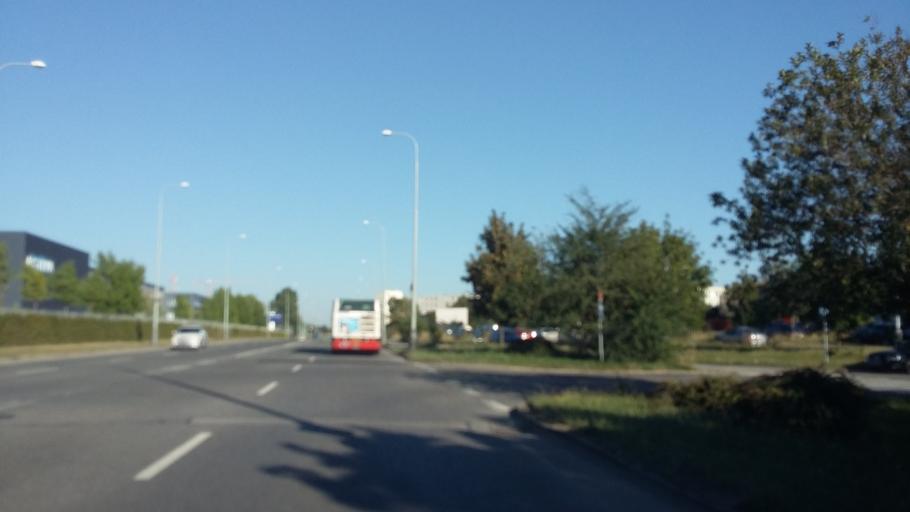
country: CZ
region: Praha
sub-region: Praha 18
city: Letnany
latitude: 50.1424
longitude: 14.5107
